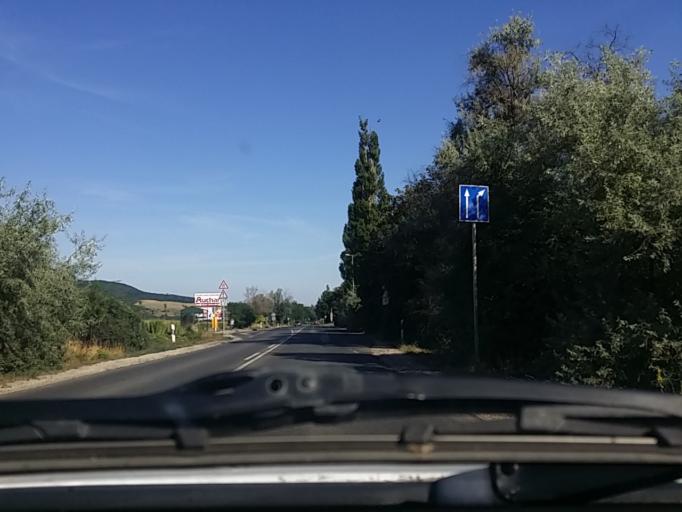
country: HU
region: Pest
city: Solymar
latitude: 47.6026
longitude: 18.9550
